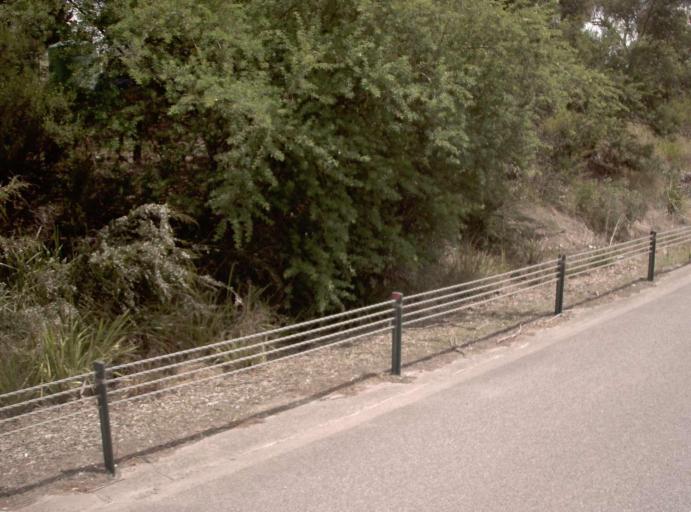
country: AU
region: Victoria
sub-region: Casey
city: Cranbourne South
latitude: -38.1378
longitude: 145.2275
